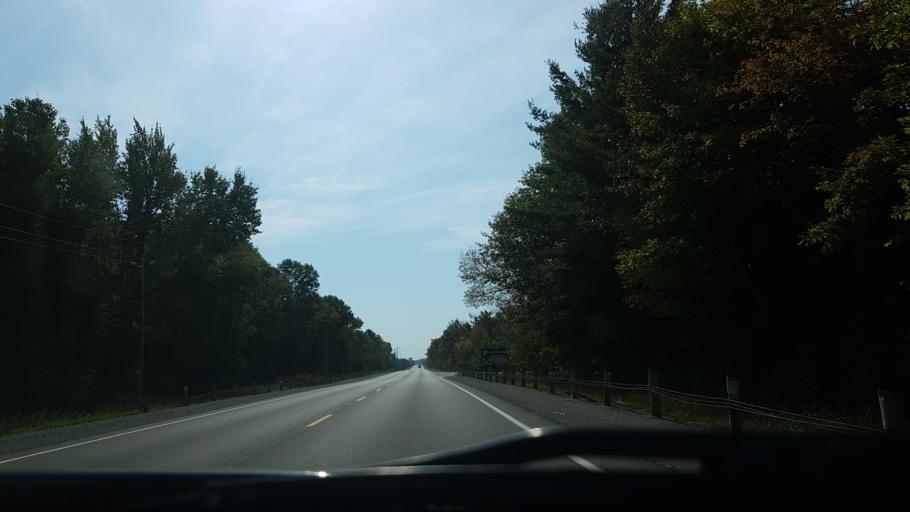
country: CA
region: Ontario
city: Orillia
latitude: 44.7205
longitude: -79.2844
